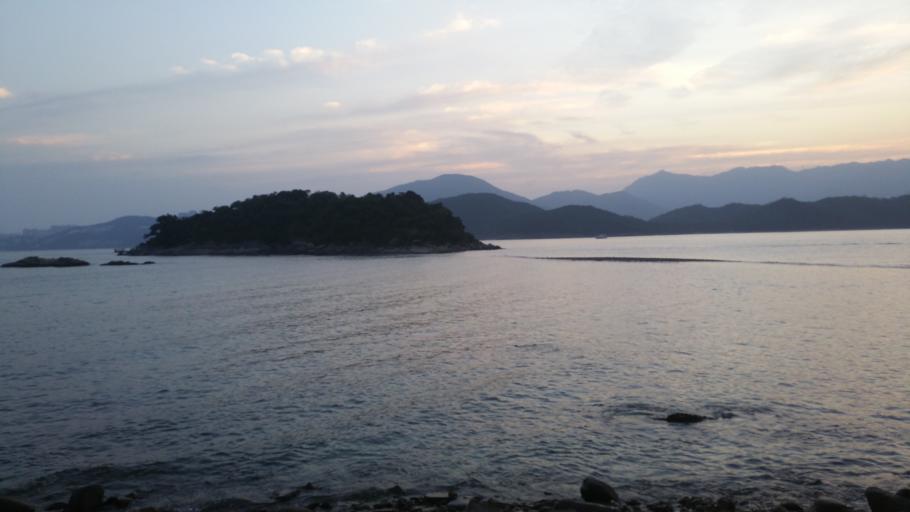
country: HK
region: Sai Kung
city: Sai Kung
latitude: 22.3658
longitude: 114.2890
